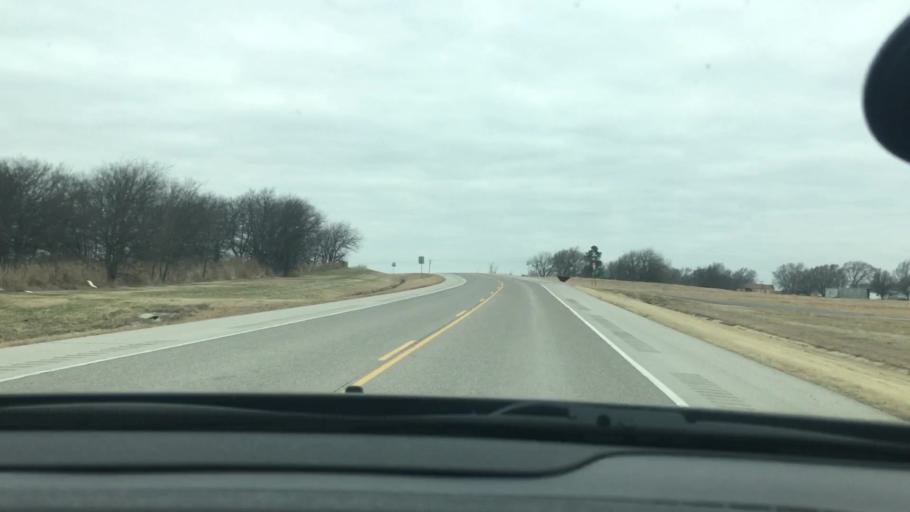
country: US
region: Oklahoma
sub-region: Garvin County
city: Wynnewood
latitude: 34.5079
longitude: -97.3491
